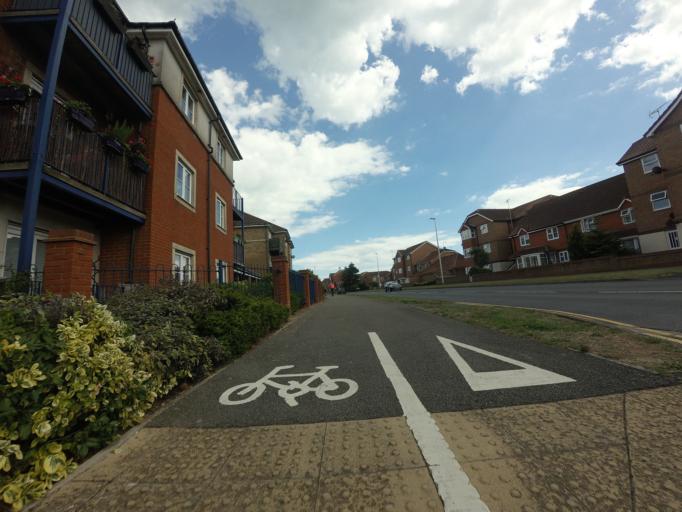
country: GB
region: England
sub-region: East Sussex
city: Pevensey
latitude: 50.7879
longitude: 0.3252
